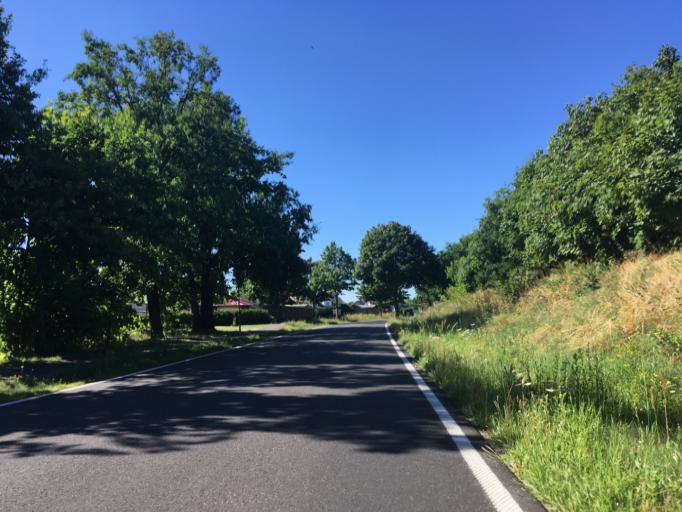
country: DE
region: Brandenburg
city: Altlandsberg
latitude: 52.5492
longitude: 13.7116
